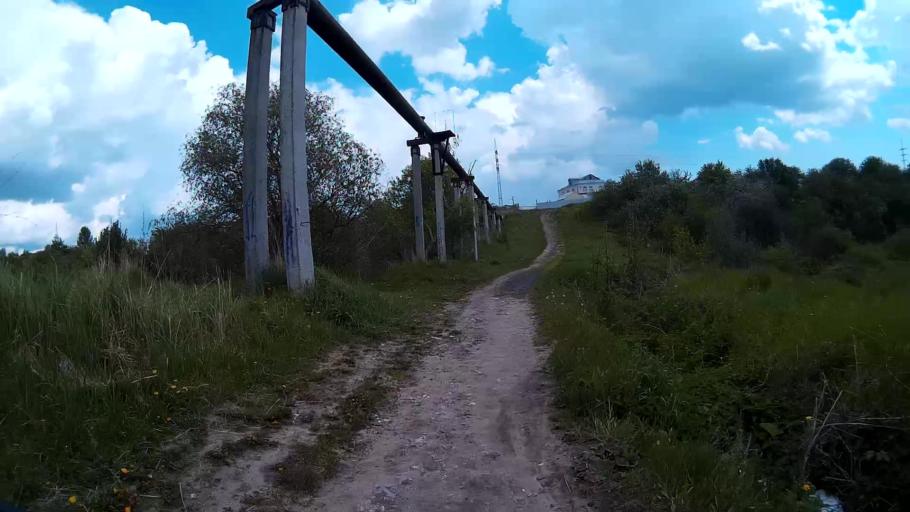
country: RU
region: Ulyanovsk
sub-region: Ulyanovskiy Rayon
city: Ulyanovsk
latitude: 54.3482
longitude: 48.3556
